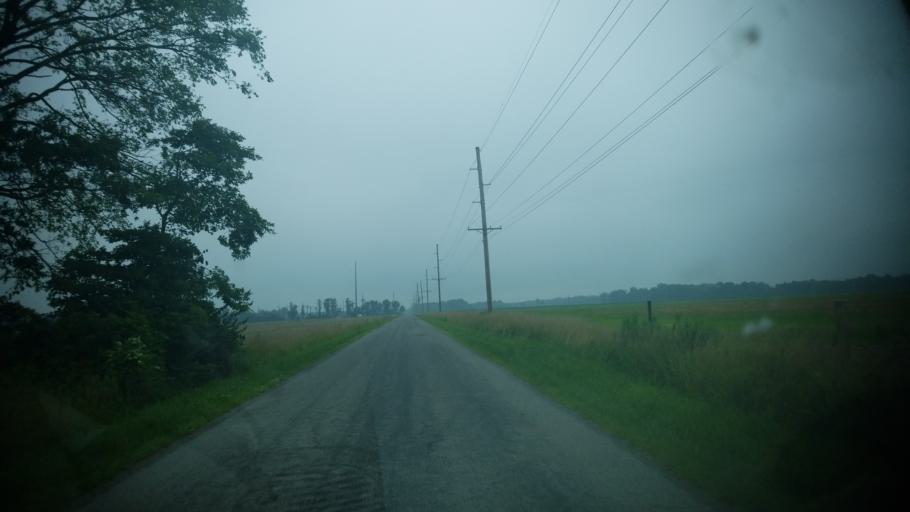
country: US
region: Illinois
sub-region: Clay County
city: Flora
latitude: 38.5407
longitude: -88.4021
